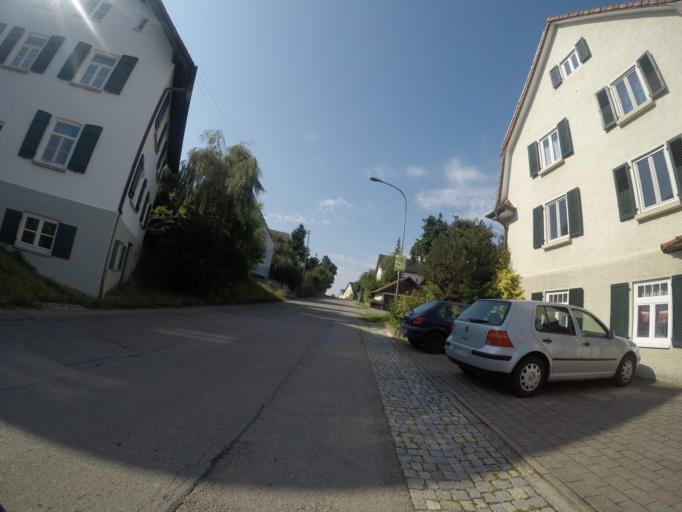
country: DE
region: Baden-Wuerttemberg
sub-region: Tuebingen Region
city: Wain
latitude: 48.1928
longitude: 10.0207
